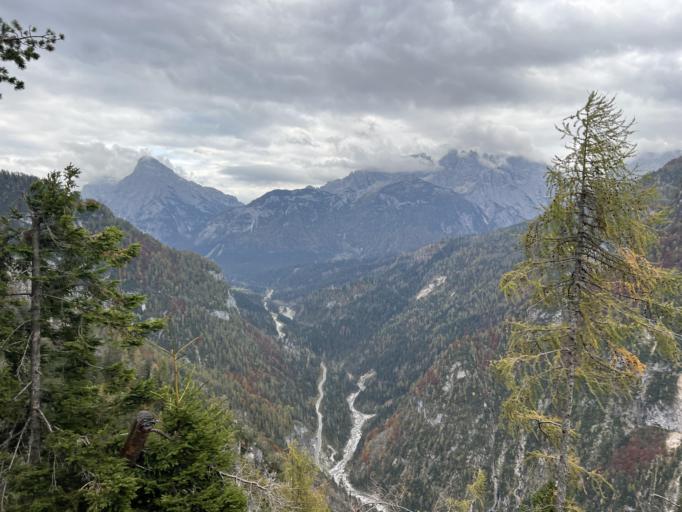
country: IT
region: Veneto
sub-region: Provincia di Belluno
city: Sappada
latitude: 46.5844
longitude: 12.6370
